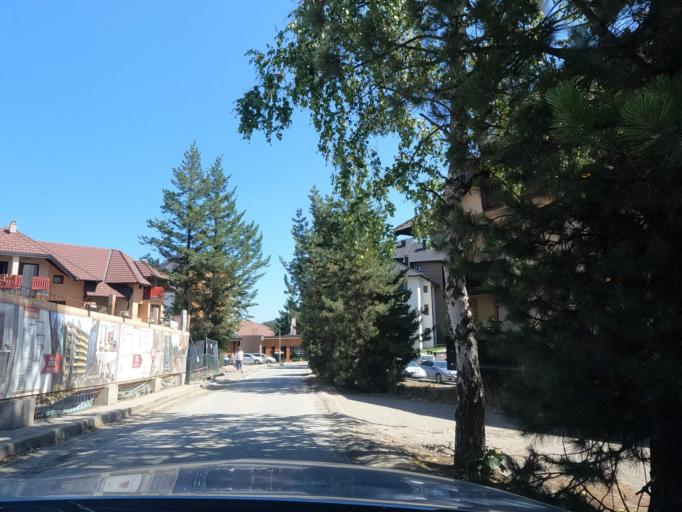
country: RS
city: Zlatibor
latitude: 43.7296
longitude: 19.6938
